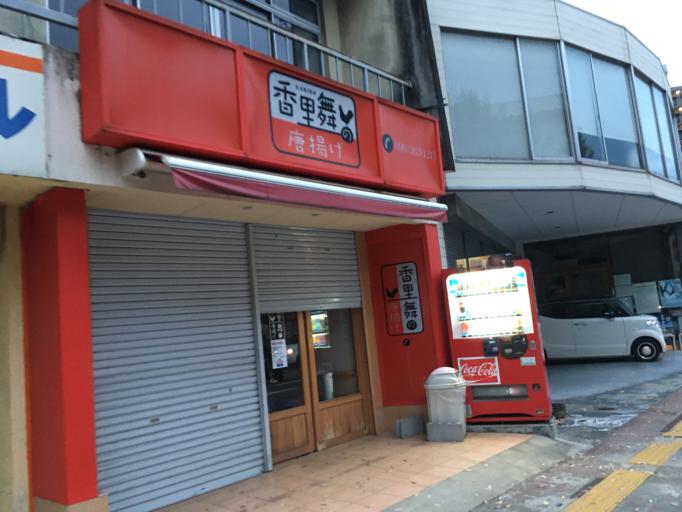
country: JP
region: Kumamoto
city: Kumamoto
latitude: 32.7979
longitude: 130.7280
